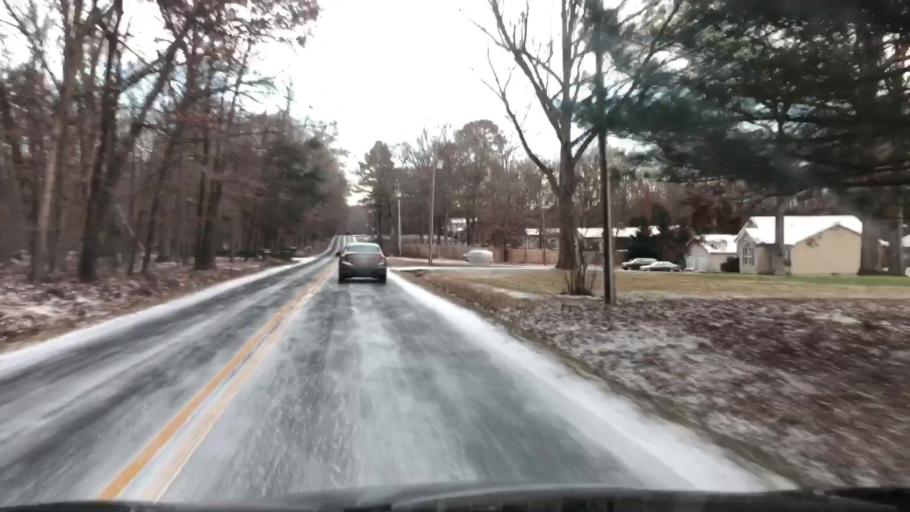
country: US
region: Virginia
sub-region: Prince William County
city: Nokesville
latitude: 38.6873
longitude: -77.6686
